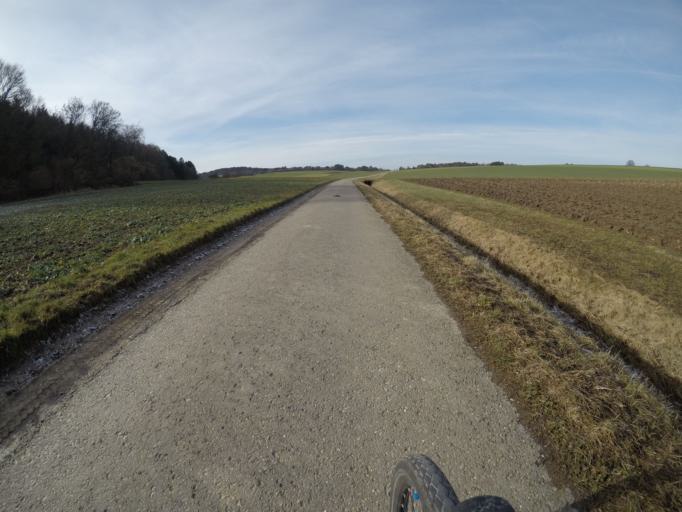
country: DE
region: Baden-Wuerttemberg
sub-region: Karlsruhe Region
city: Althengstett
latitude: 48.6943
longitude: 8.7979
